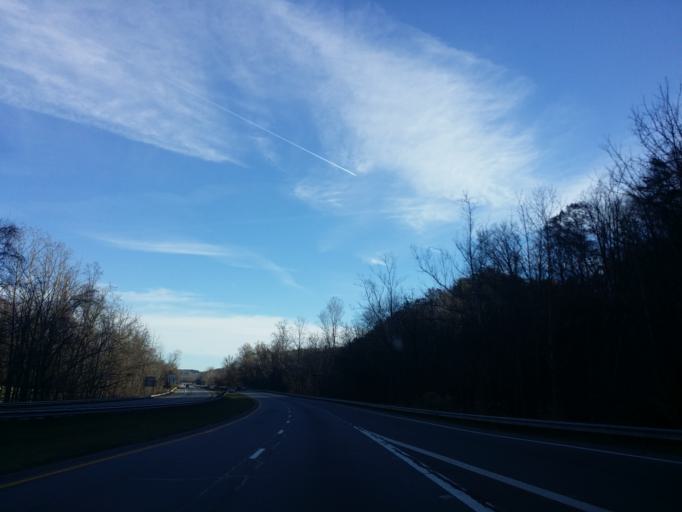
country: US
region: North Carolina
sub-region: Buncombe County
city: Black Mountain
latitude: 35.6236
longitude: -82.1785
